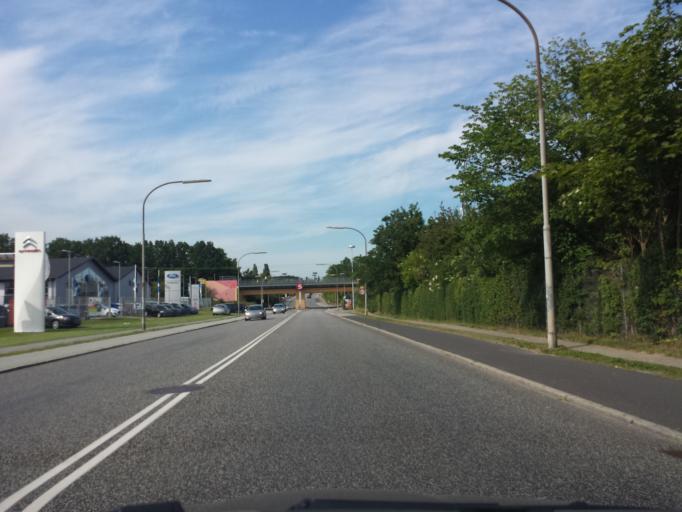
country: DK
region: Capital Region
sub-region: Ballerup Kommune
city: Ballerup
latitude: 55.7232
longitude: 12.3853
